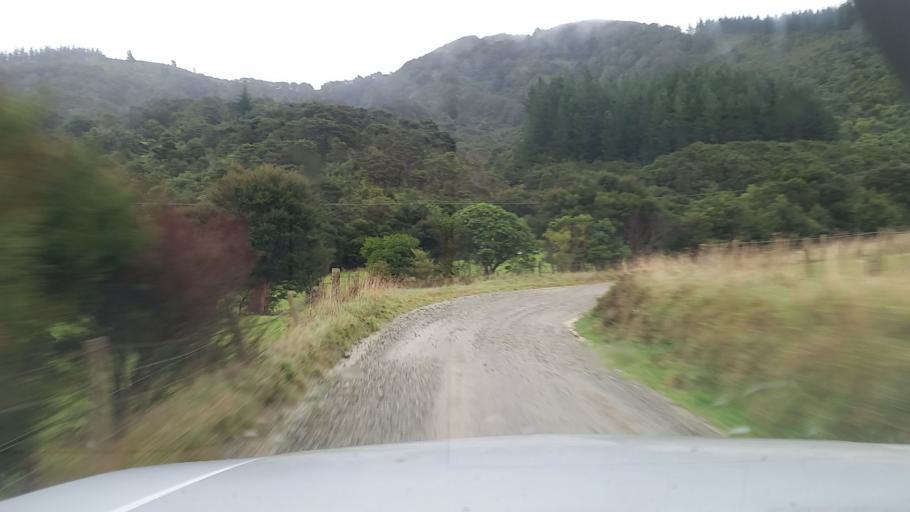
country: NZ
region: Marlborough
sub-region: Marlborough District
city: Picton
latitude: -41.1481
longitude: 174.0508
